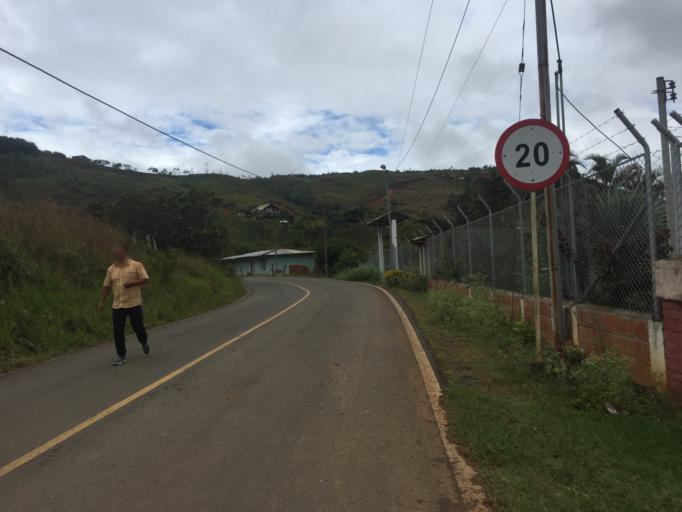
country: CO
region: Valle del Cauca
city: Dagua
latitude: 3.6878
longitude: -76.5928
